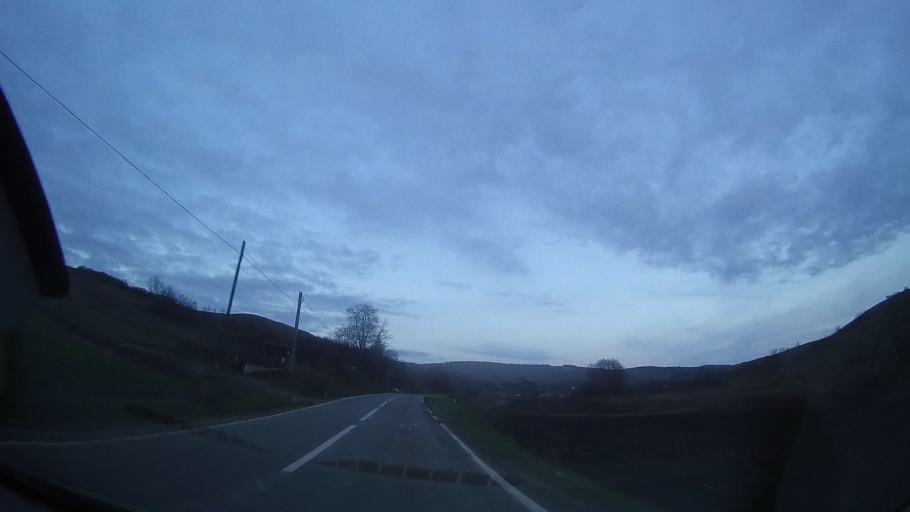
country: RO
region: Cluj
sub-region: Comuna Caianu
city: Vaida-Camaras
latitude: 46.8009
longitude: 23.9557
